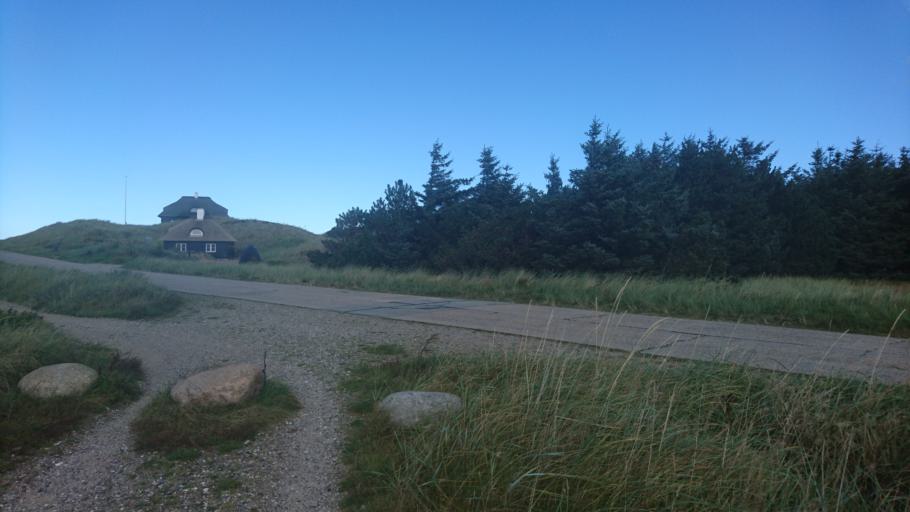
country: DK
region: North Denmark
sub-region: Frederikshavn Kommune
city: Skagen
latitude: 57.7234
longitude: 10.5285
